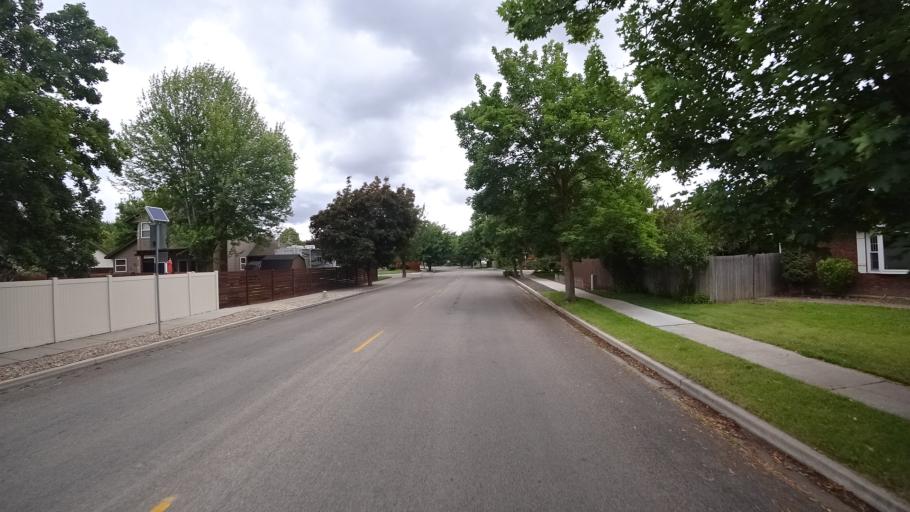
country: US
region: Idaho
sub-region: Ada County
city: Garden City
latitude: 43.6611
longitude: -116.2517
